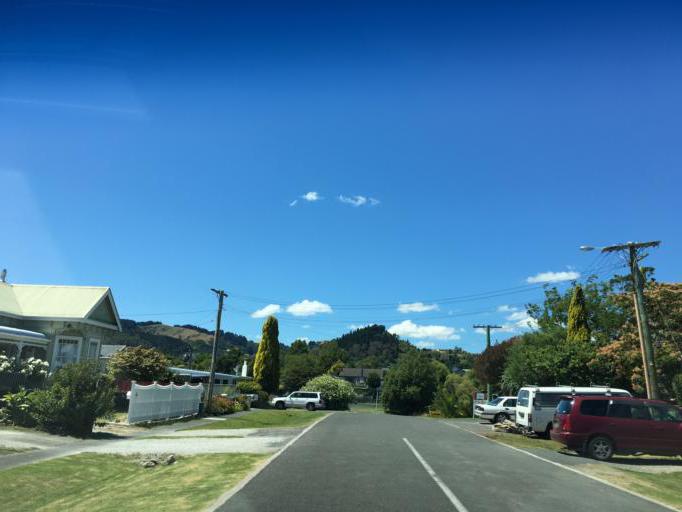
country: NZ
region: Gisborne
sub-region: Gisborne District
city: Gisborne
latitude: -38.6598
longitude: 178.0244
